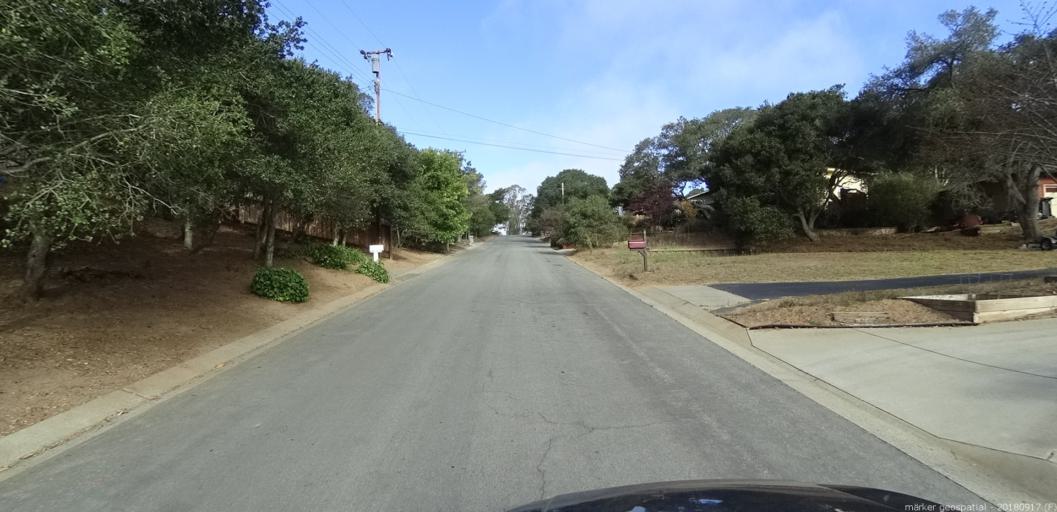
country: US
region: California
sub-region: Monterey County
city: Elkhorn
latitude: 36.8152
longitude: -121.7078
